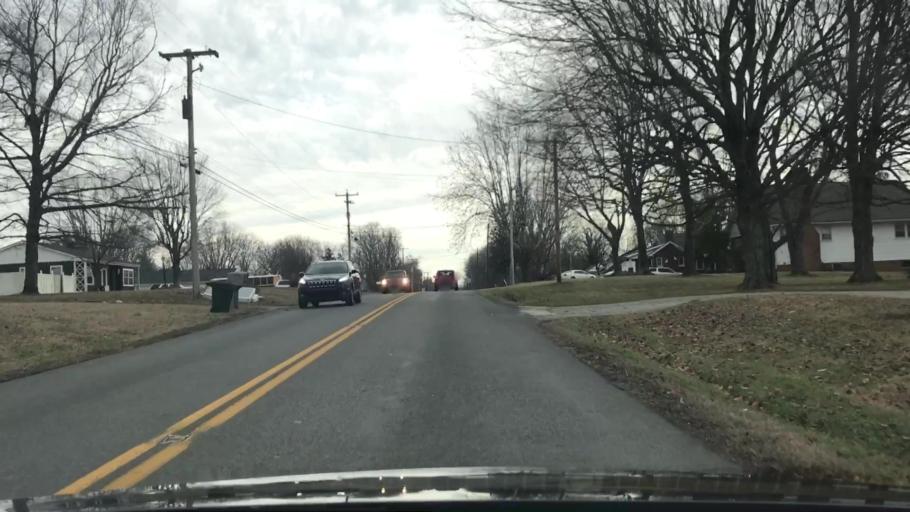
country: US
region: Kentucky
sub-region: Christian County
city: Hopkinsville
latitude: 36.8606
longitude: -87.5112
